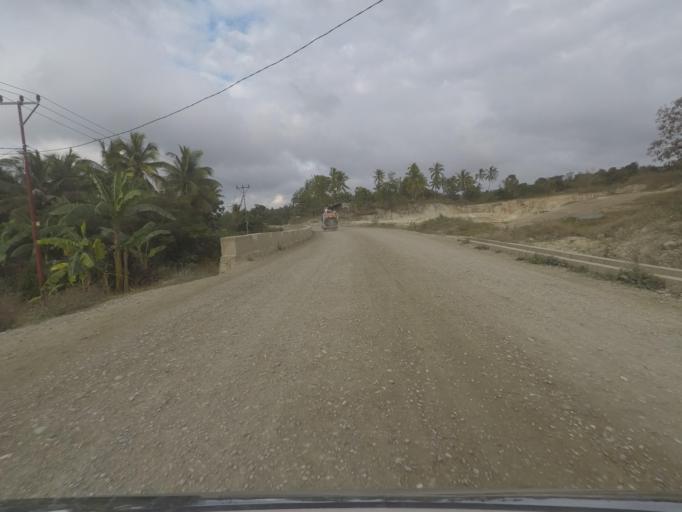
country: TL
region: Baucau
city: Baucau
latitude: -8.5123
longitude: 126.4422
